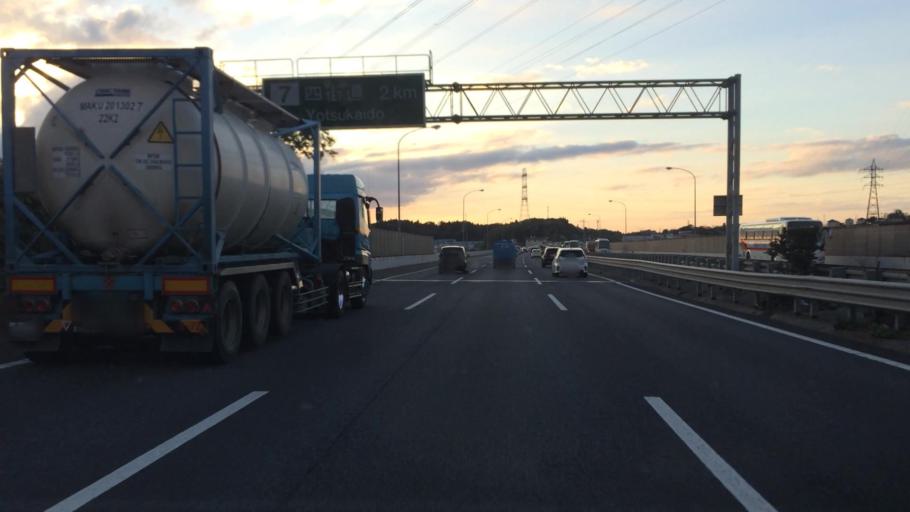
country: JP
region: Chiba
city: Sakura
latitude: 35.6822
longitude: 140.2056
